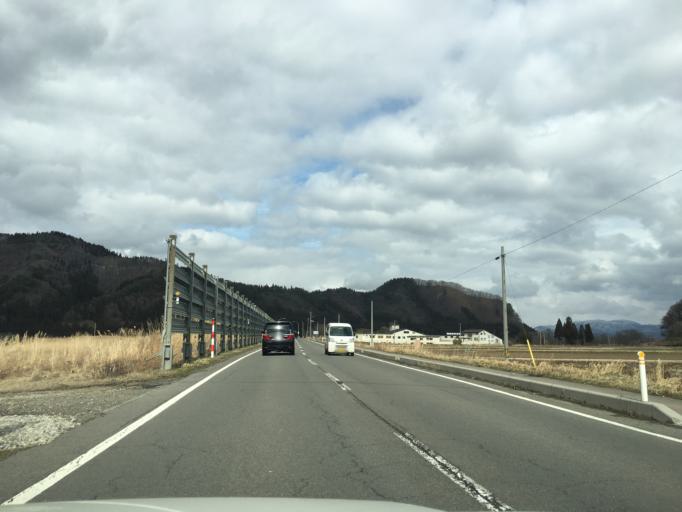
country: JP
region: Akita
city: Hanawa
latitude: 40.2402
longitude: 140.7383
